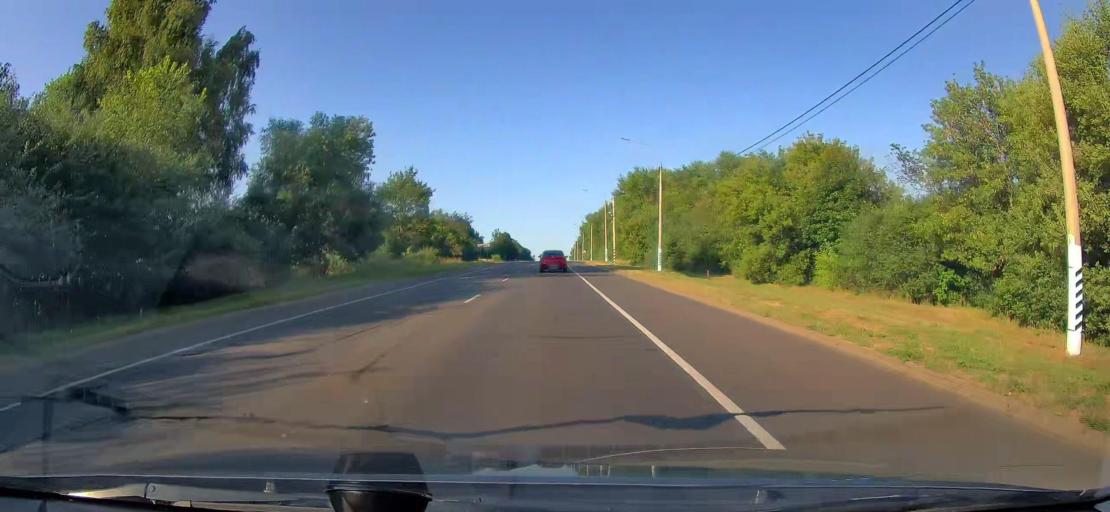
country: RU
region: Tula
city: Plavsk
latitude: 53.6216
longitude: 37.1922
